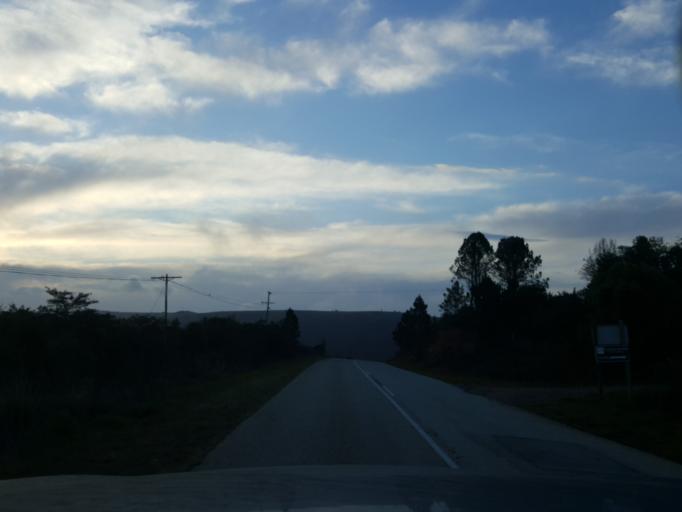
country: ZA
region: Eastern Cape
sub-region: Cacadu District Municipality
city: Grahamstown
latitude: -33.3835
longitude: 26.4707
